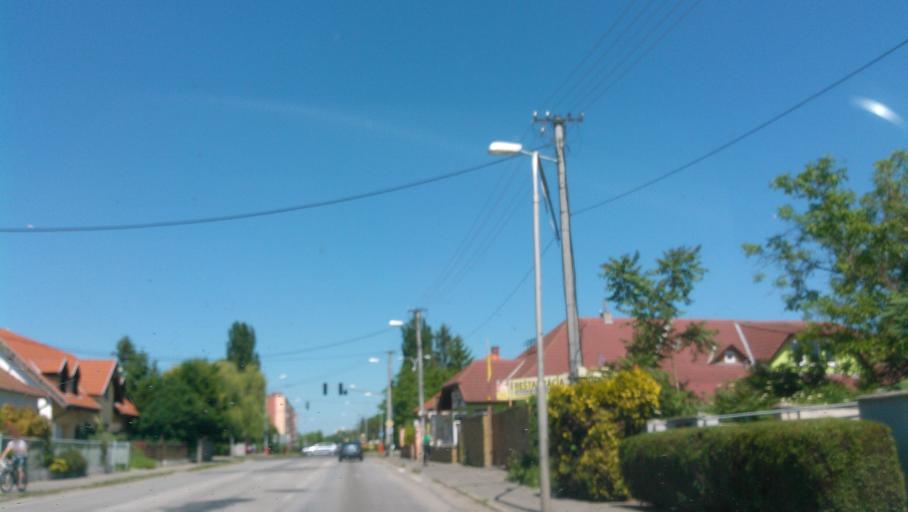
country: SK
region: Nitriansky
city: Sellye
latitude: 48.1528
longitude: 17.8704
